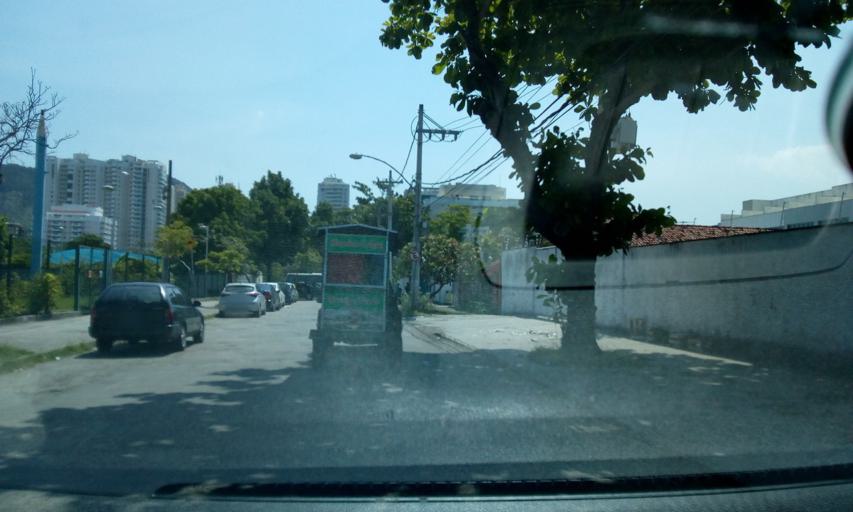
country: BR
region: Rio de Janeiro
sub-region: Nilopolis
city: Nilopolis
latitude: -23.0195
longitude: -43.4819
